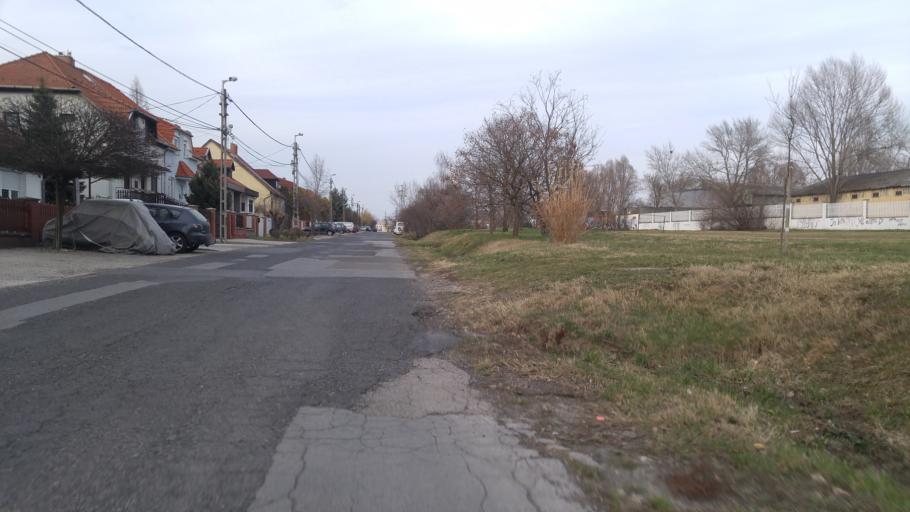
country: HU
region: Budapest
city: Budapest XVII. keruelet
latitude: 47.4723
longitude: 19.2366
